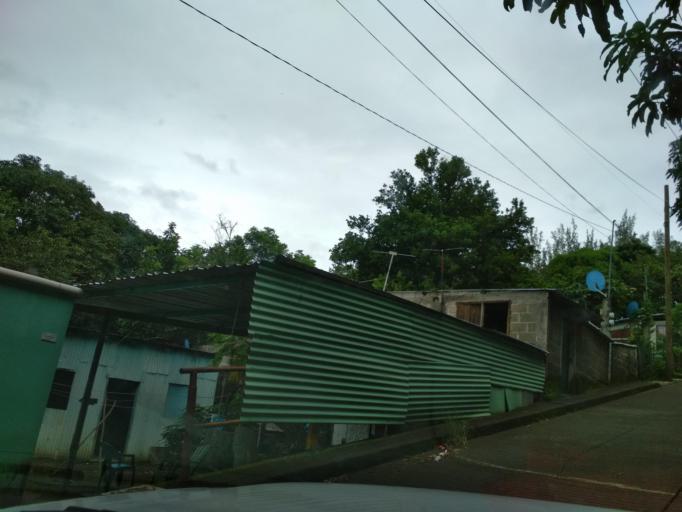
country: MX
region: Veracruz
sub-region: San Andres Tuxtla
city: Los Pinos
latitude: 18.4468
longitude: -95.2321
